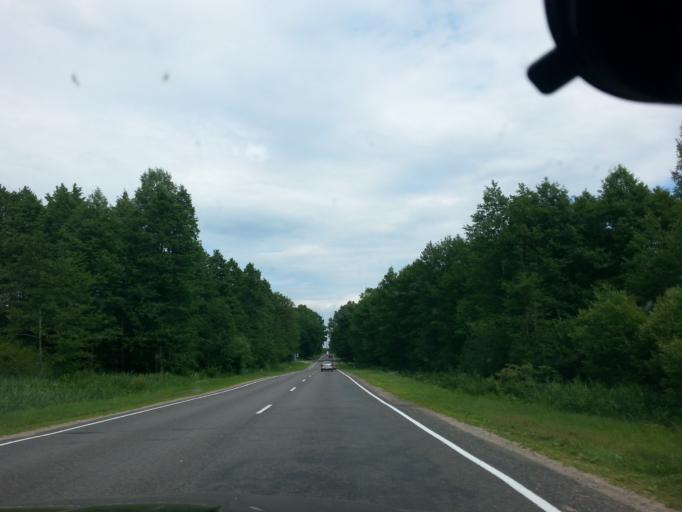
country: BY
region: Minsk
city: Narach
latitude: 54.8865
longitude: 26.8150
